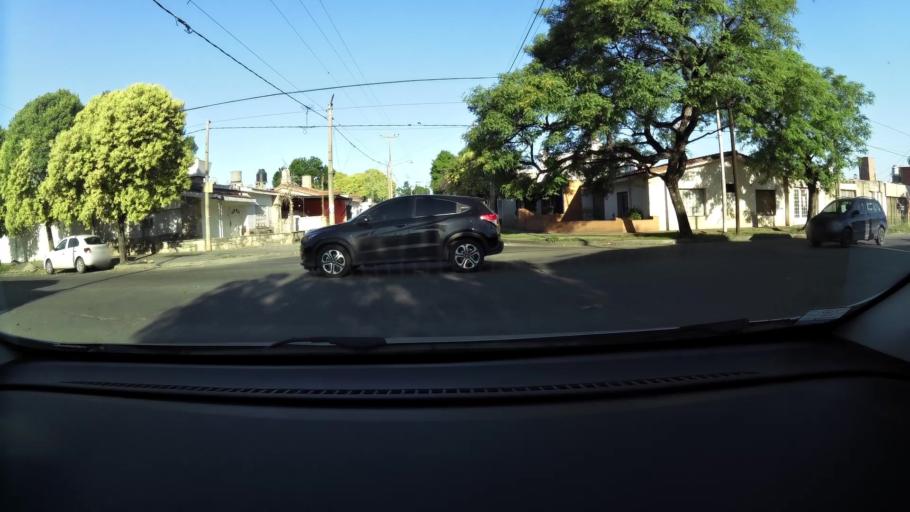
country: AR
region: Cordoba
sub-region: Departamento de Capital
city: Cordoba
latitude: -31.3771
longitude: -64.1963
